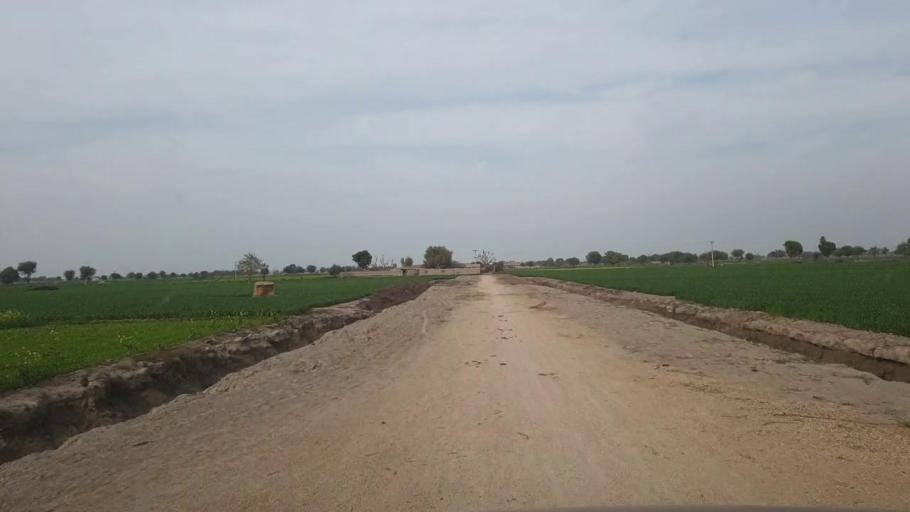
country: PK
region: Sindh
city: Shahpur Chakar
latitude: 26.1197
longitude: 68.5131
